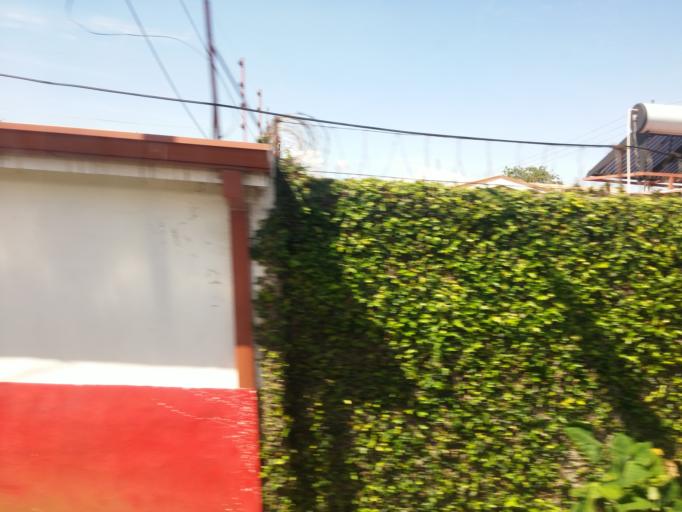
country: CR
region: Heredia
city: Mercedes
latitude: 9.9995
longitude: -84.1414
